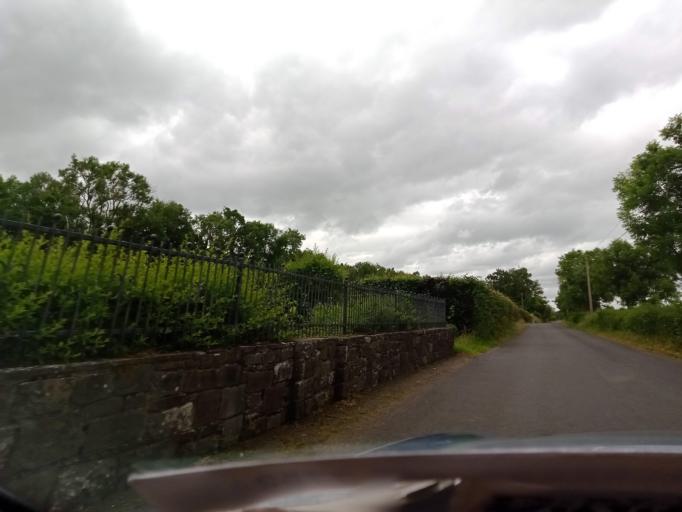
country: IE
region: Leinster
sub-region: Kilkenny
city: Thomastown
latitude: 52.5822
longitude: -7.1867
